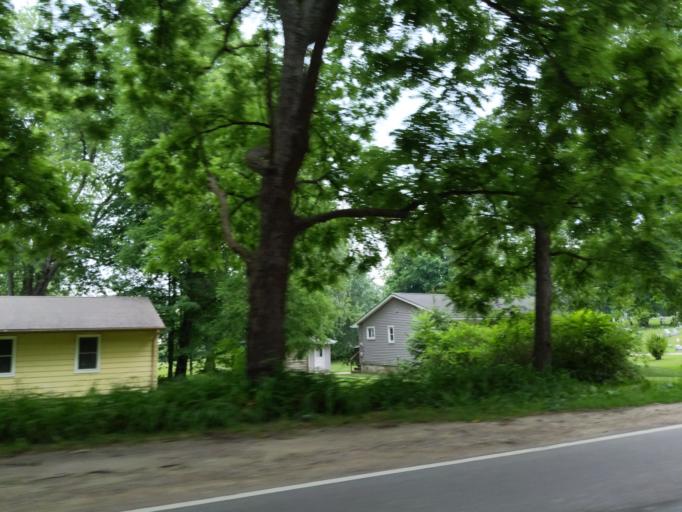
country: US
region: Michigan
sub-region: Livingston County
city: Whitmore Lake
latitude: 42.4441
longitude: -83.8025
